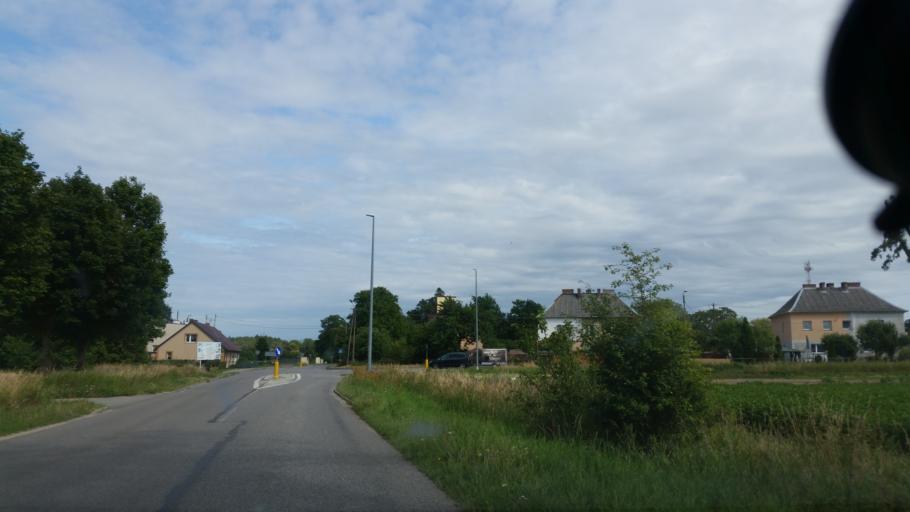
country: PL
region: Pomeranian Voivodeship
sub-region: Powiat wejherowski
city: Choczewo
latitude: 54.7252
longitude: 17.8547
